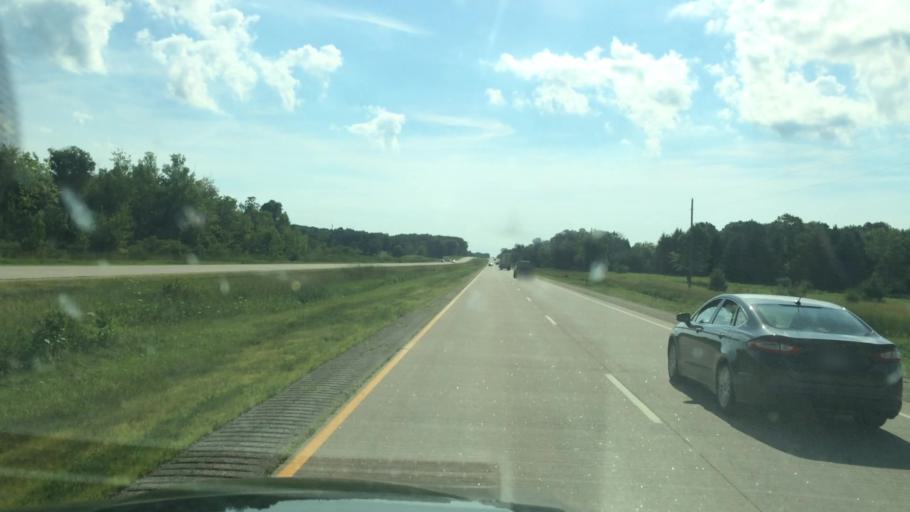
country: US
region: Wisconsin
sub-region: Waupaca County
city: Marion
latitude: 44.8039
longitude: -88.9938
